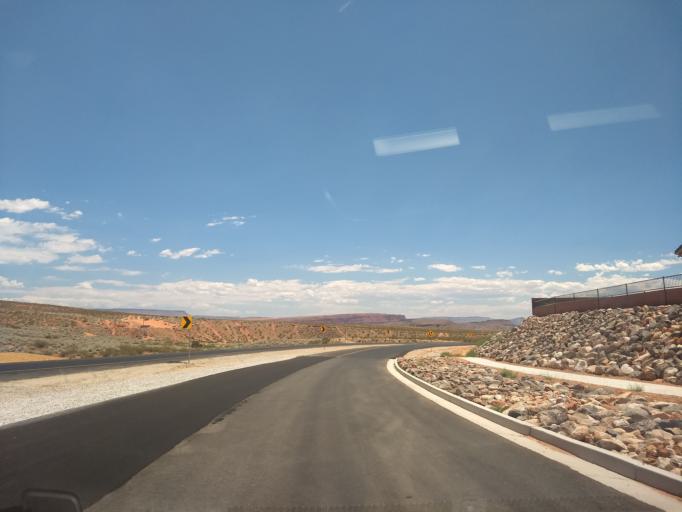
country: US
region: Utah
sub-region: Washington County
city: Washington
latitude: 37.1590
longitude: -113.5204
